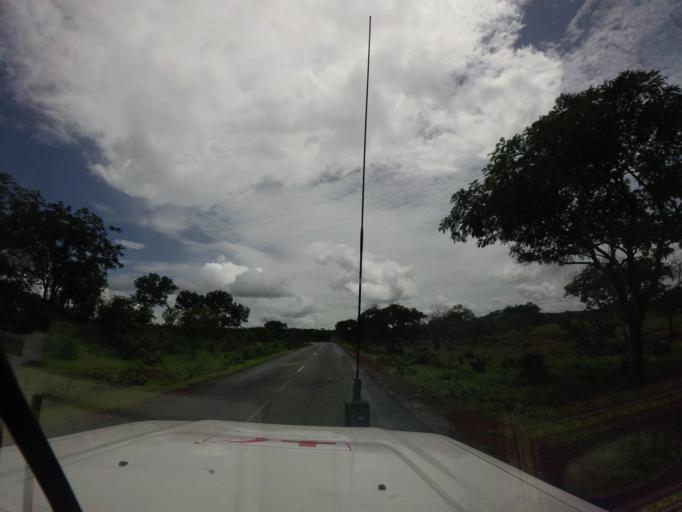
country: GN
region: Faranah
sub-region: Faranah Prefecture
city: Faranah
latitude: 10.0147
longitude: -10.9291
